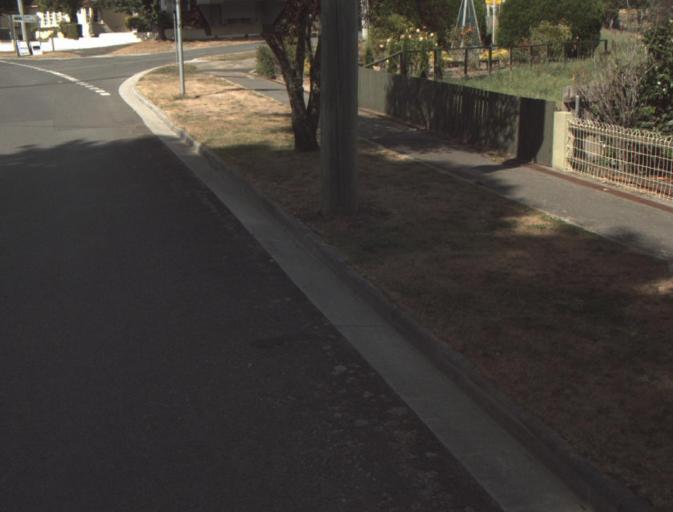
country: AU
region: Tasmania
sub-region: Launceston
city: Mayfield
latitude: -41.2532
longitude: 147.2158
